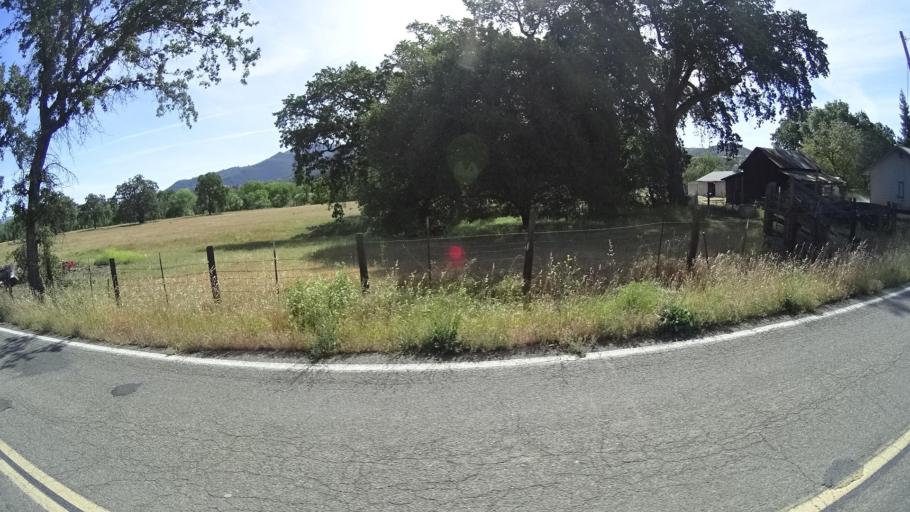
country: US
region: California
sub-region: Lake County
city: Kelseyville
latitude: 38.9681
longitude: -122.8386
